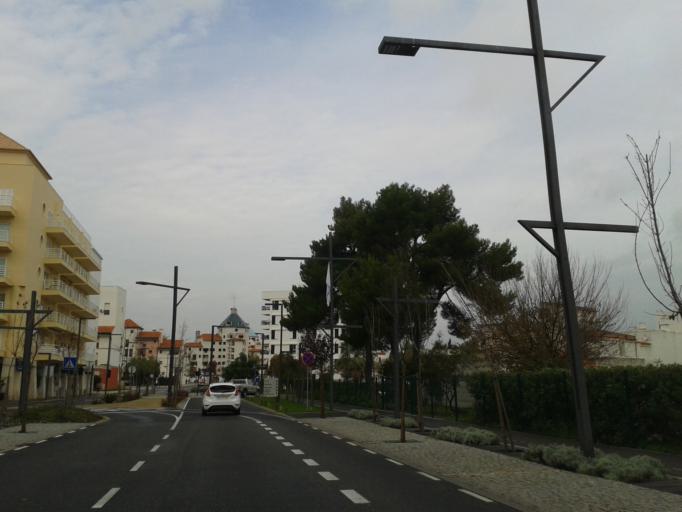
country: PT
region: Faro
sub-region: Loule
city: Vilamoura
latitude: 37.0776
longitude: -8.1151
